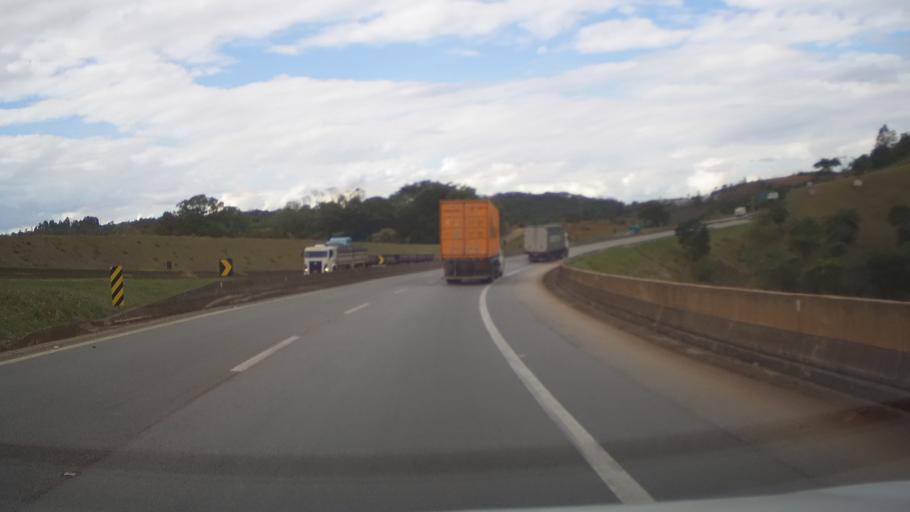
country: BR
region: Minas Gerais
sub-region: Igarape
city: Igarape
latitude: -20.2865
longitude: -44.4351
